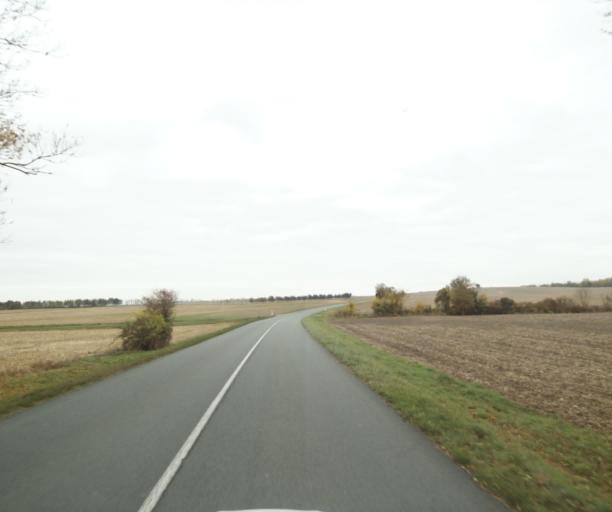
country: FR
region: Poitou-Charentes
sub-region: Departement de la Charente-Maritime
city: Les Gonds
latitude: 45.7119
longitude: -0.6444
